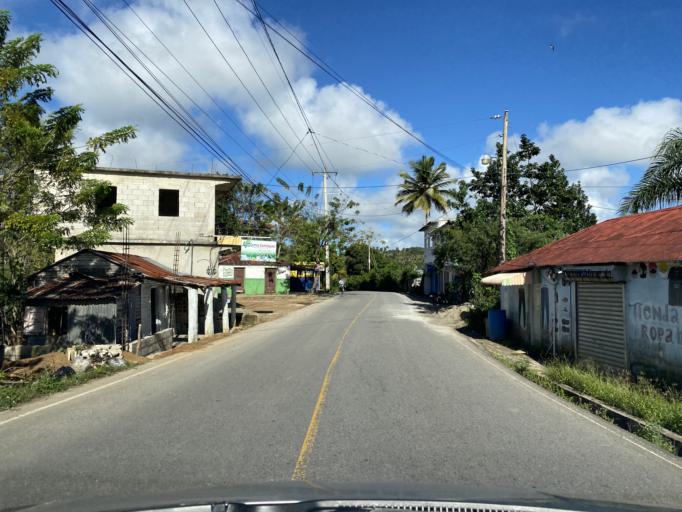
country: DO
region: Samana
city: Sanchez
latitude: 19.2522
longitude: -69.5826
